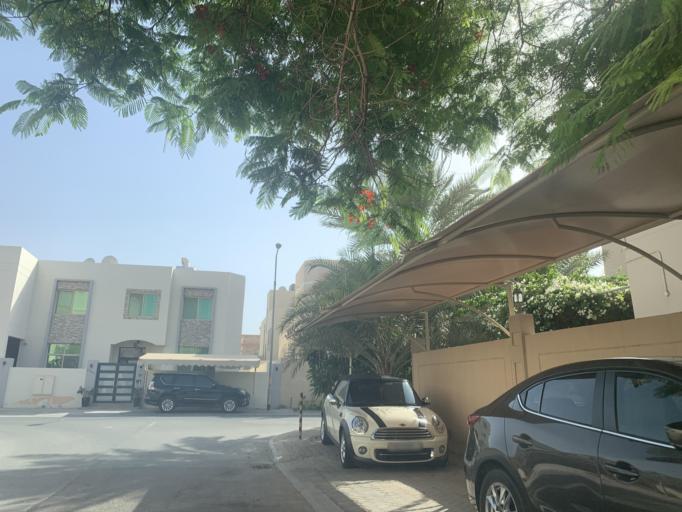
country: BH
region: Northern
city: Madinat `Isa
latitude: 26.1645
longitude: 50.5745
